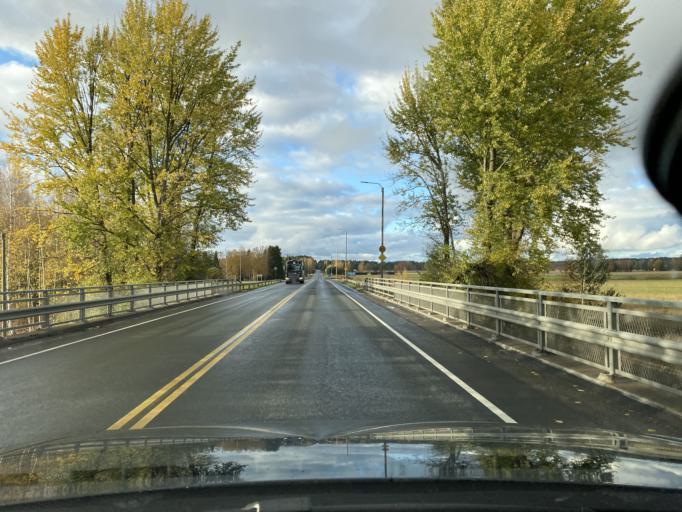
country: FI
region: Haeme
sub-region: Forssa
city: Humppila
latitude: 60.9534
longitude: 23.3397
